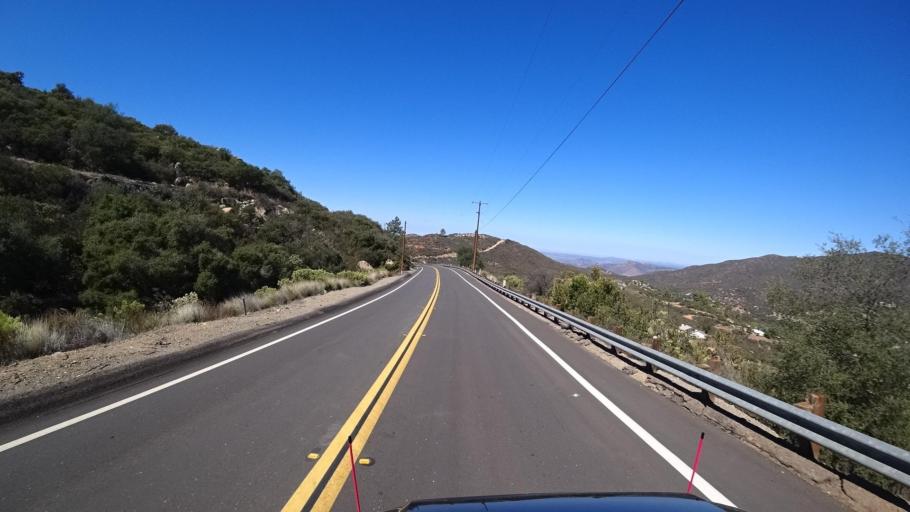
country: US
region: California
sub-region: San Diego County
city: Jamul
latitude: 32.7340
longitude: -116.7998
